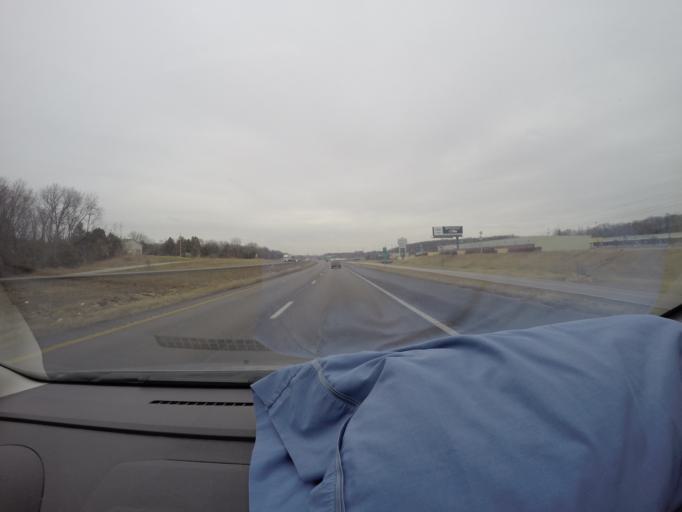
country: US
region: Missouri
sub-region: Warren County
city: Warrenton
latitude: 38.8195
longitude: -91.1662
